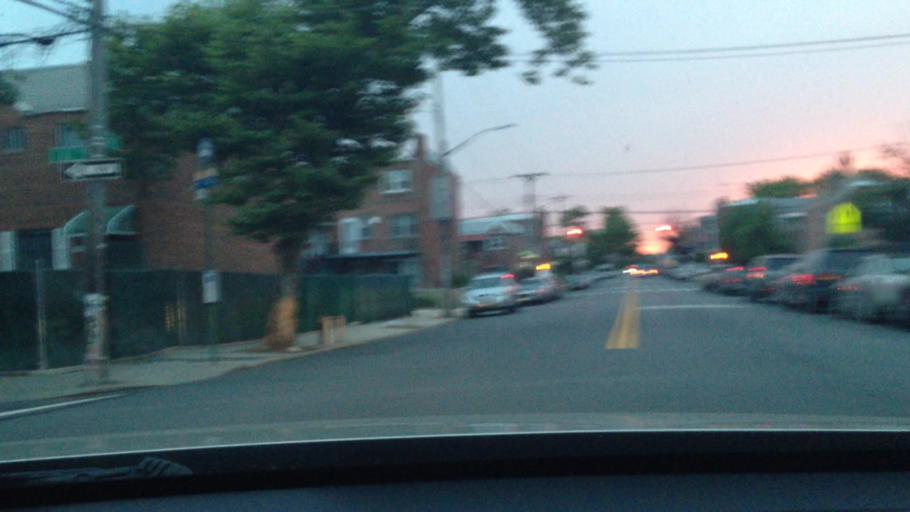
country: US
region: New York
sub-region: Kings County
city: East New York
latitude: 40.6315
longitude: -73.9064
